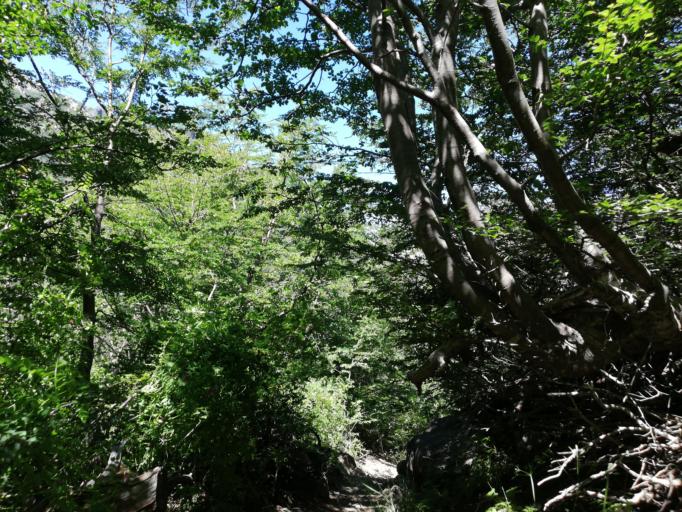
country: AR
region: Neuquen
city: Villa La Angostura
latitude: -41.1903
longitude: -71.8365
